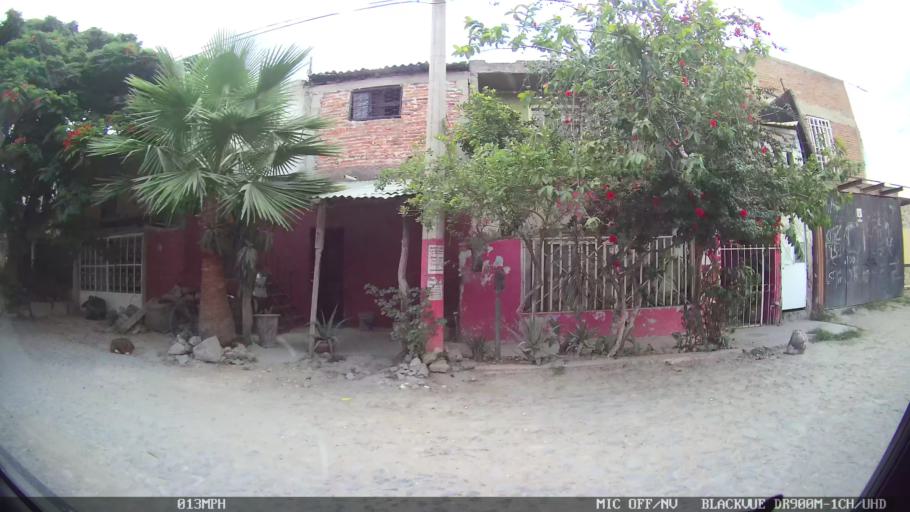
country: MX
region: Jalisco
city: Tonala
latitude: 20.6559
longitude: -103.2537
